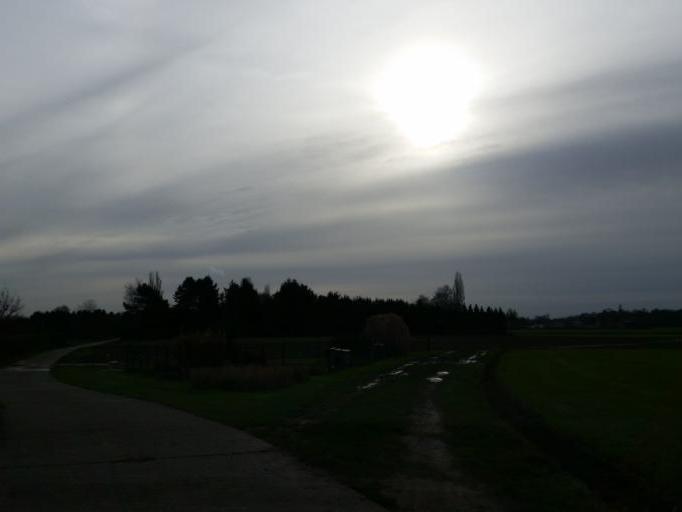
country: BE
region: Flanders
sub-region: Provincie Vlaams-Brabant
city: Zemst
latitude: 50.9930
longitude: 4.4509
